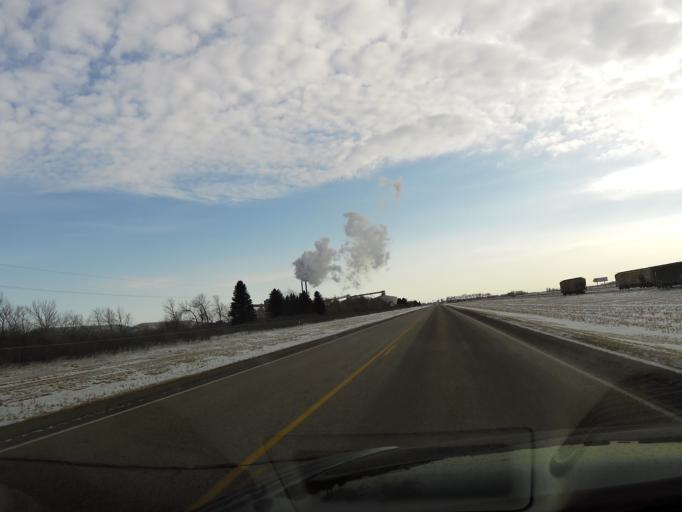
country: US
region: Minnesota
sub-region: Kittson County
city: Hallock
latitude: 48.5992
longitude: -97.1787
